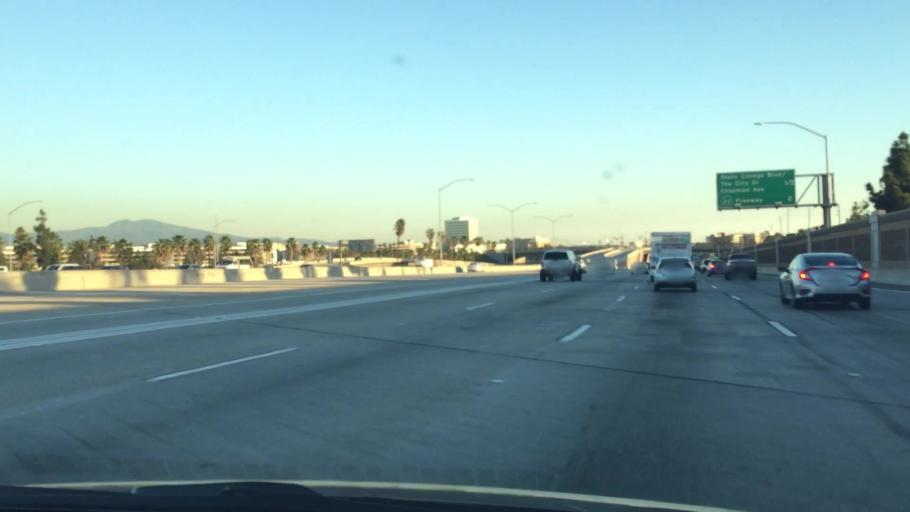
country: US
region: California
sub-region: Orange County
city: Anaheim
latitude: 33.8031
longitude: -117.9025
